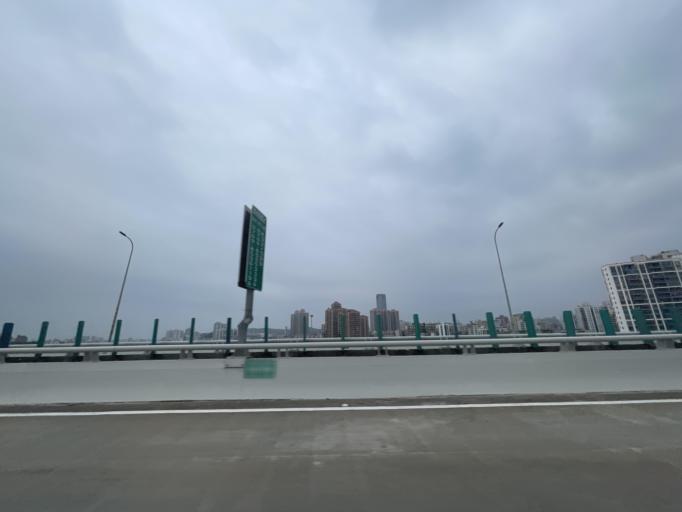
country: CN
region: Guangdong
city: Humen
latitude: 22.8067
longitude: 113.6673
